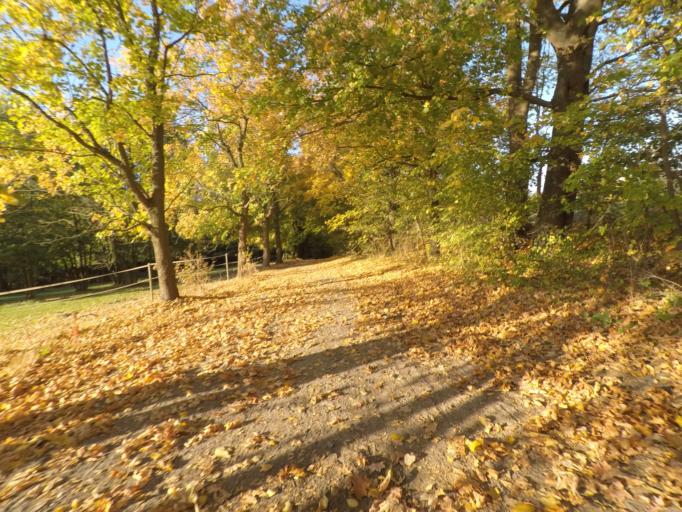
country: DE
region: Brandenburg
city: Biesenthal
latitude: 52.7792
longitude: 13.6409
